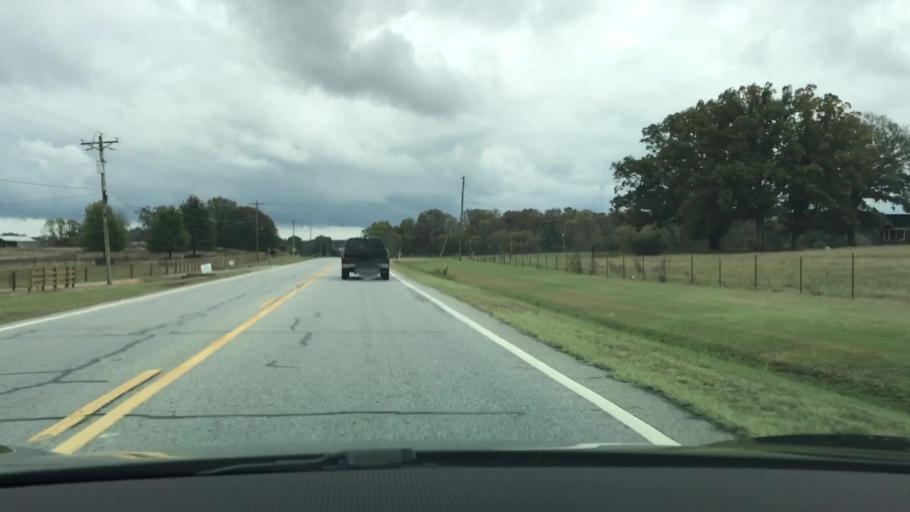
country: US
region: Georgia
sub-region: Oconee County
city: Watkinsville
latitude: 33.8262
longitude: -83.3725
